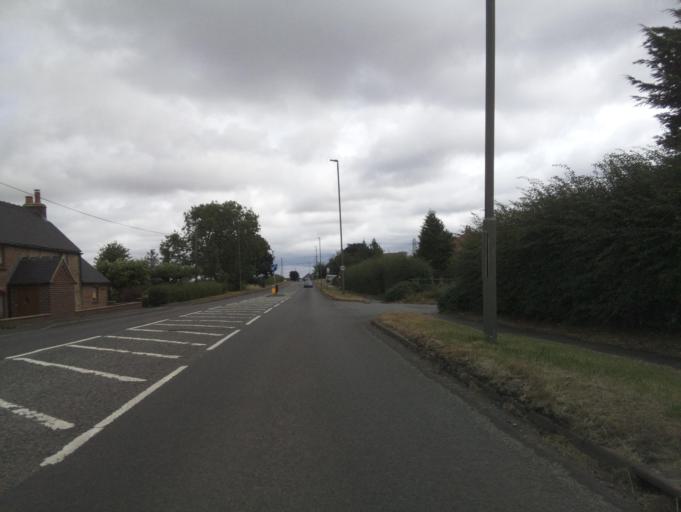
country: GB
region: England
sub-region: Derbyshire
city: Heanor
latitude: 53.0036
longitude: -1.3849
